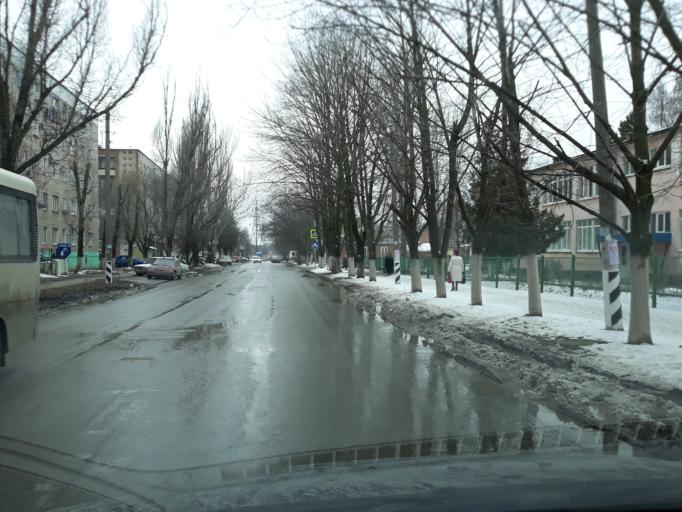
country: RU
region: Rostov
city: Taganrog
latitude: 47.2329
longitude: 38.8792
